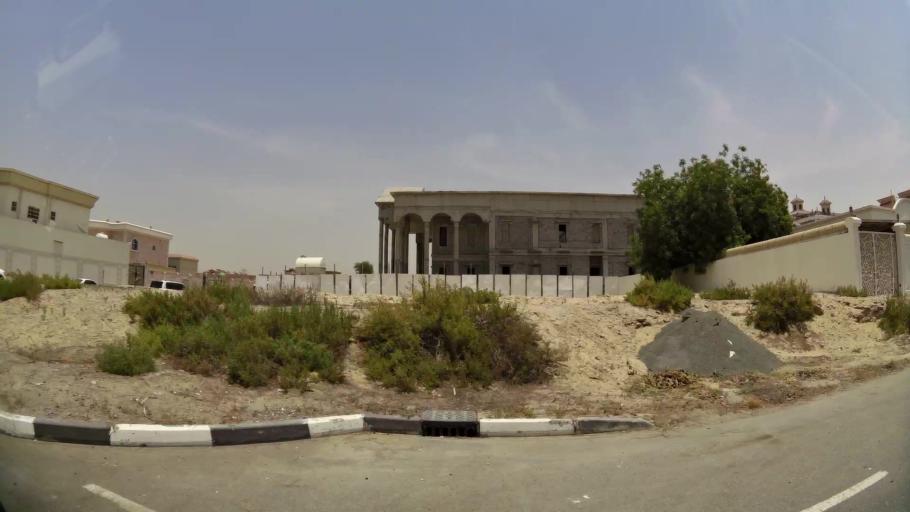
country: AE
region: Ash Shariqah
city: Sharjah
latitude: 25.2098
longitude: 55.3896
